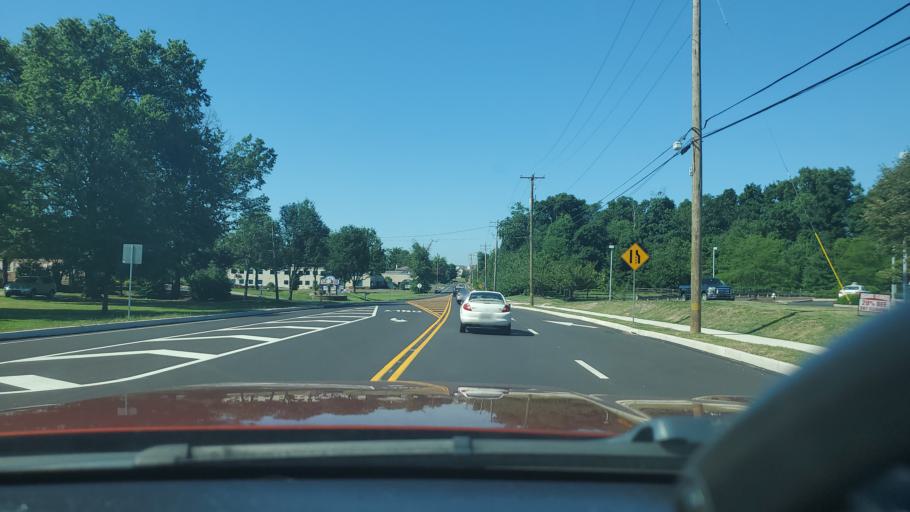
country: US
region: Pennsylvania
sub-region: Montgomery County
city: Limerick
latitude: 40.2317
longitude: -75.5282
